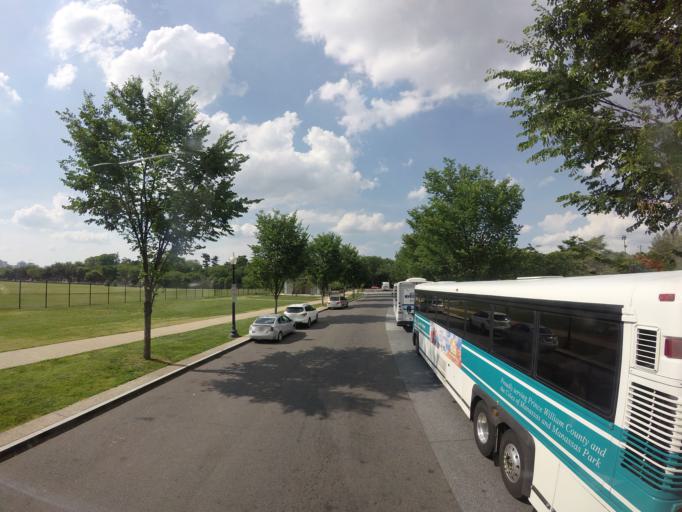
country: US
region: Washington, D.C.
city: Washington, D.C.
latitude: 38.8855
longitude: -77.0450
